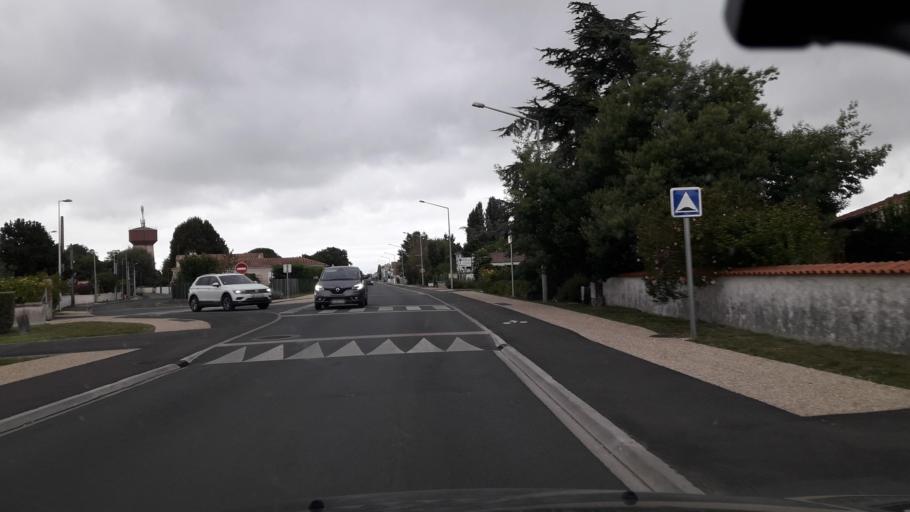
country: FR
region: Poitou-Charentes
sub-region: Departement de la Charente-Maritime
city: Arvert
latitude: 45.7412
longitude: -1.1181
